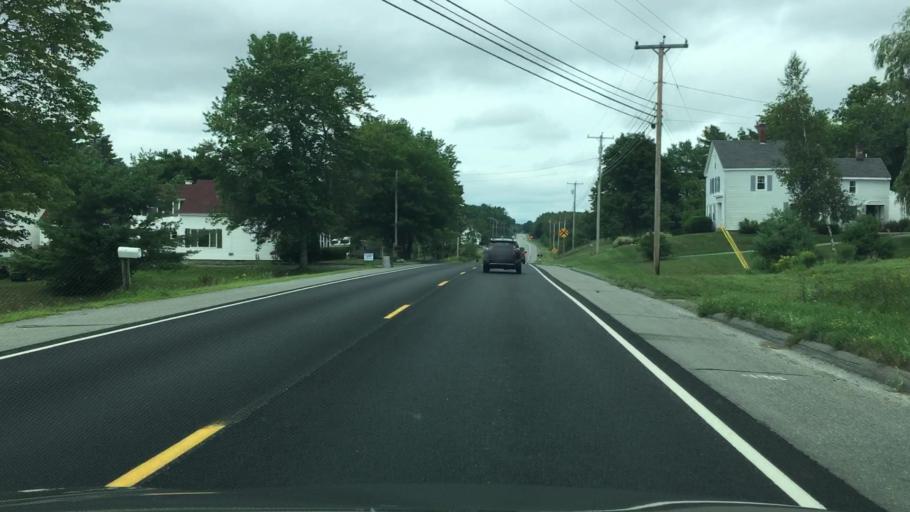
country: US
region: Maine
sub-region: Penobscot County
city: Orrington
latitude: 44.7004
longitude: -68.8209
